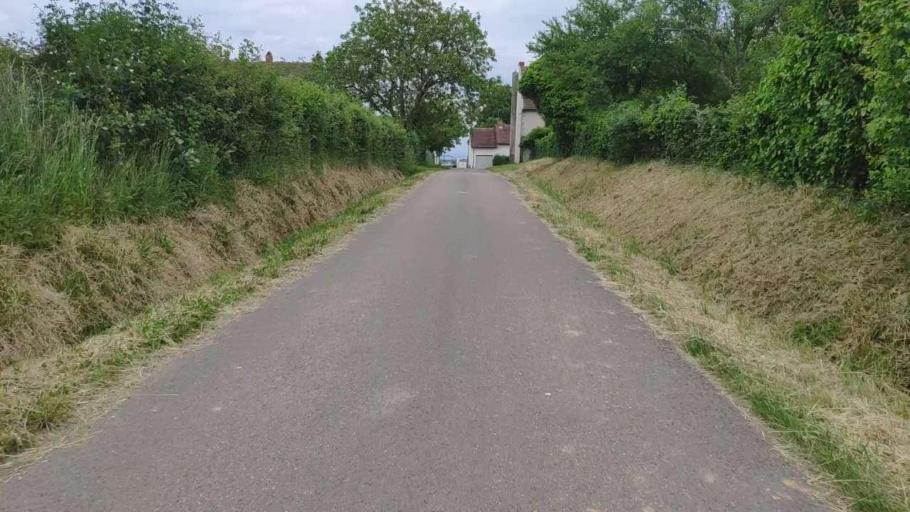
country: FR
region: Franche-Comte
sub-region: Departement du Jura
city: Bletterans
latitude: 46.7878
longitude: 5.5068
